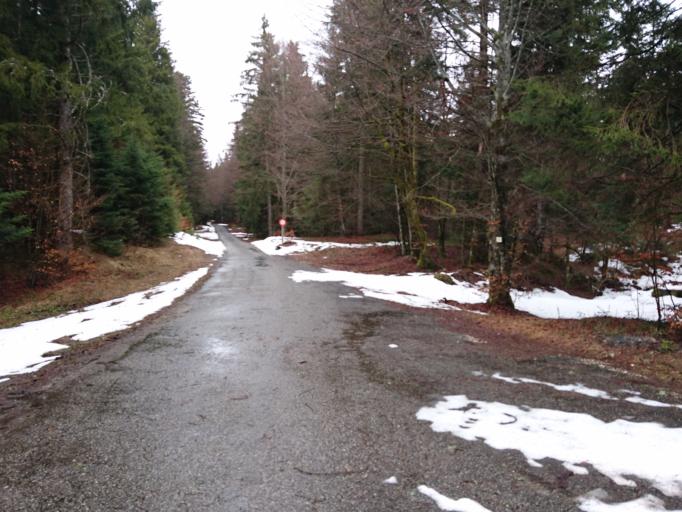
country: FR
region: Rhone-Alpes
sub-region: Departement de l'Ain
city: Martignat
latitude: 46.1973
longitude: 5.6704
